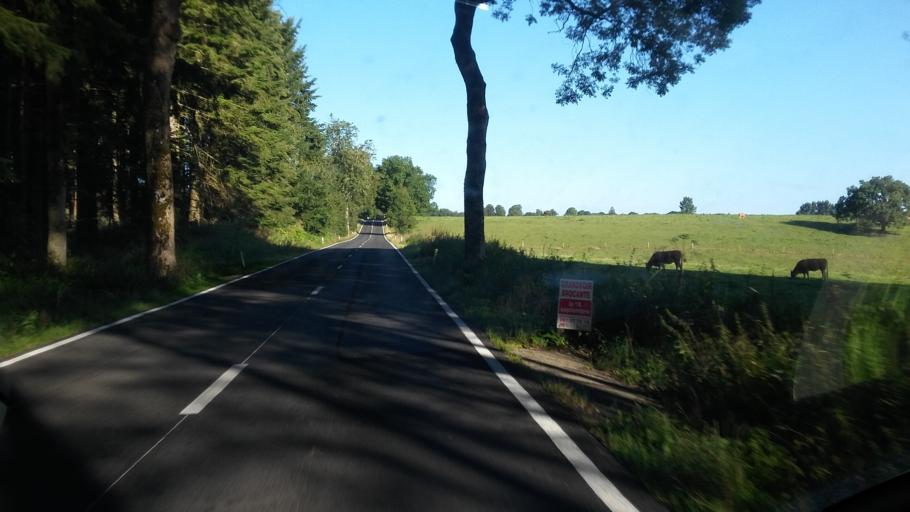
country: BE
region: Wallonia
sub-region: Province du Luxembourg
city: Leglise
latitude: 49.8168
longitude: 5.4992
